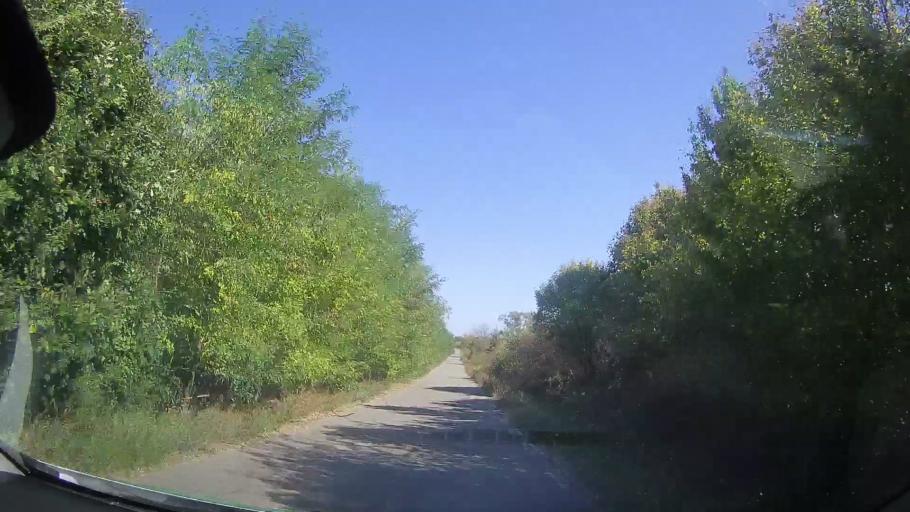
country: RO
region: Timis
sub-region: Comuna Ohaba Lunga
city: Ohaba Lunga
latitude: 45.9151
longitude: 21.9524
